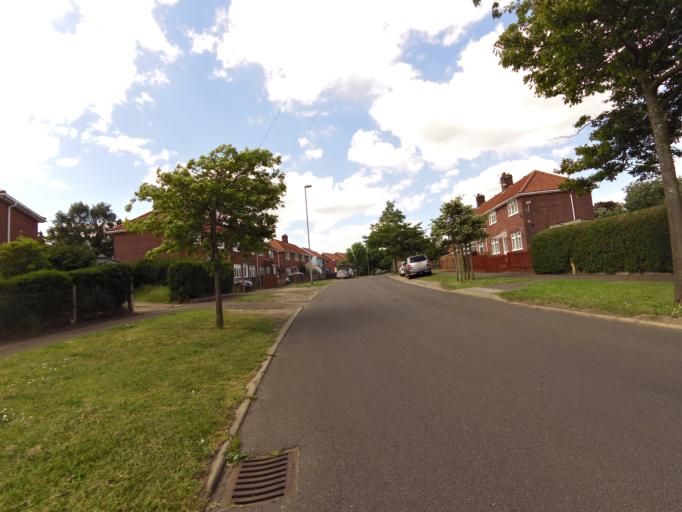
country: GB
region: England
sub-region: Norfolk
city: Norwich
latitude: 52.6483
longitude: 1.2701
